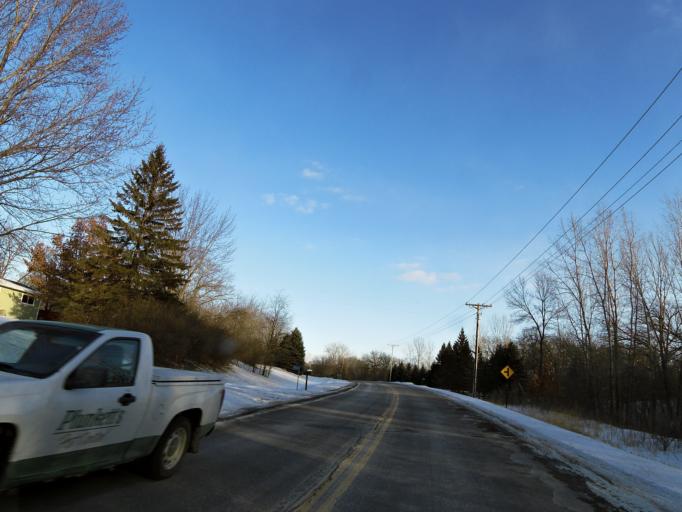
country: US
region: Minnesota
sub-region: Dakota County
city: Lakeville
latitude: 44.6527
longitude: -93.3221
